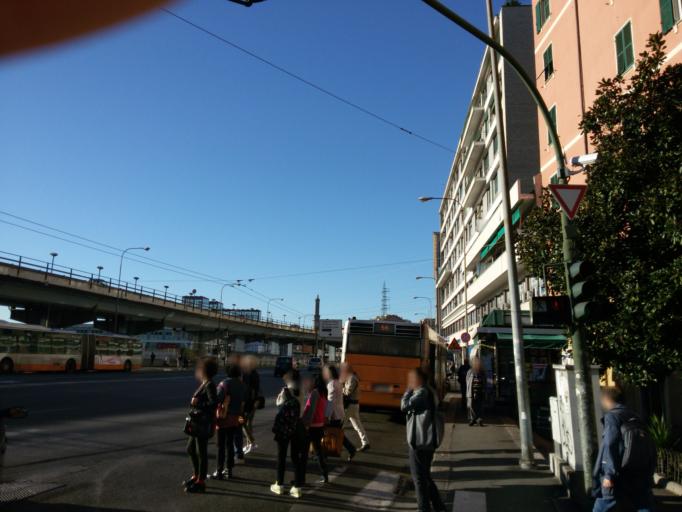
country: IT
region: Liguria
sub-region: Provincia di Genova
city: San Teodoro
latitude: 44.4129
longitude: 8.9097
